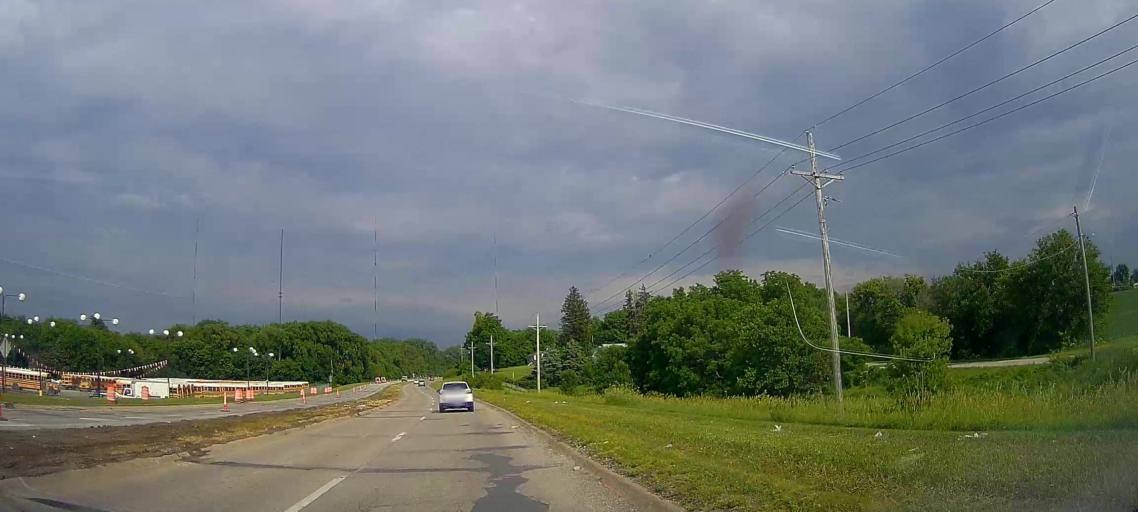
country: US
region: Nebraska
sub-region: Douglas County
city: Ralston
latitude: 41.3101
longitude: -96.0453
